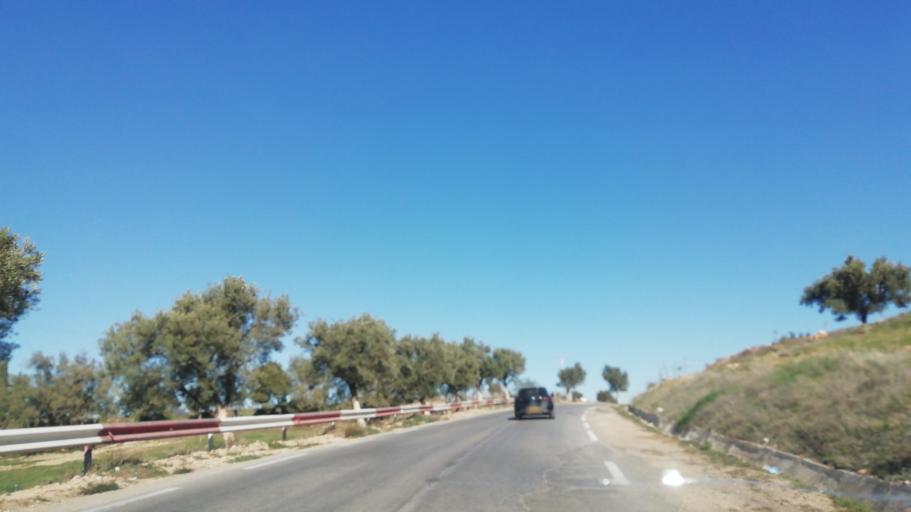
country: DZ
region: Tlemcen
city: Beni Mester
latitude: 34.8328
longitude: -1.5047
